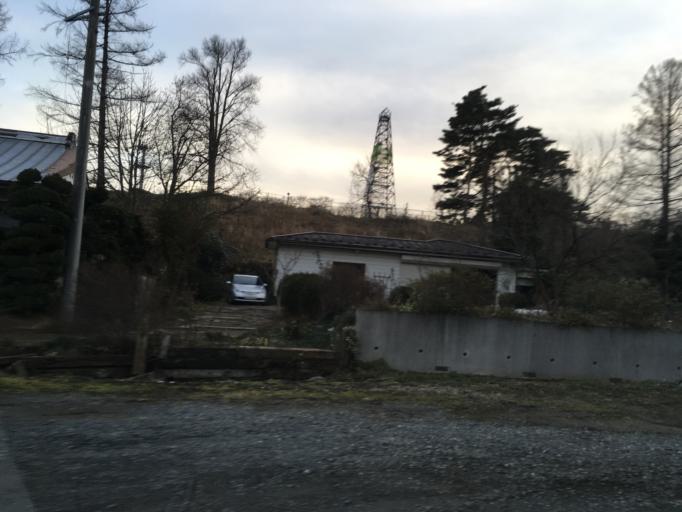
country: JP
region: Miyagi
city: Kogota
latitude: 38.6533
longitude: 141.0692
